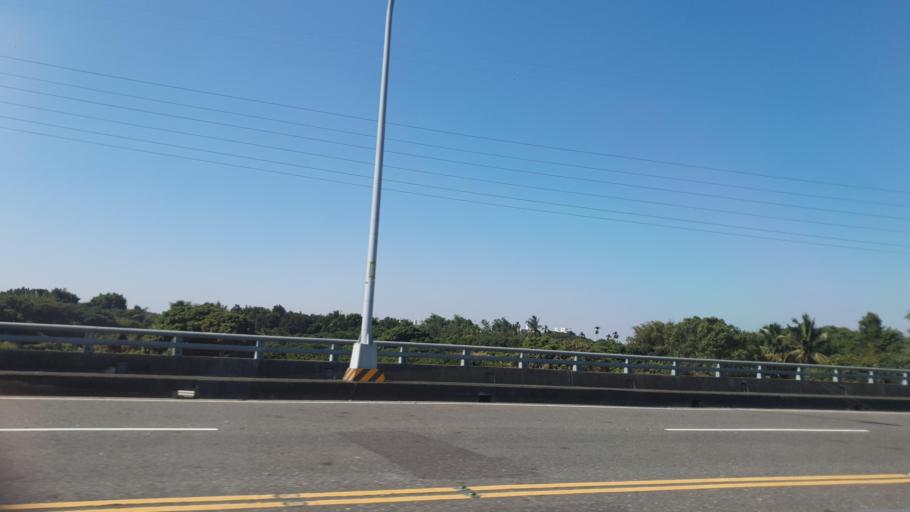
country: TW
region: Taiwan
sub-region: Tainan
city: Tainan
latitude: 23.0338
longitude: 120.3220
